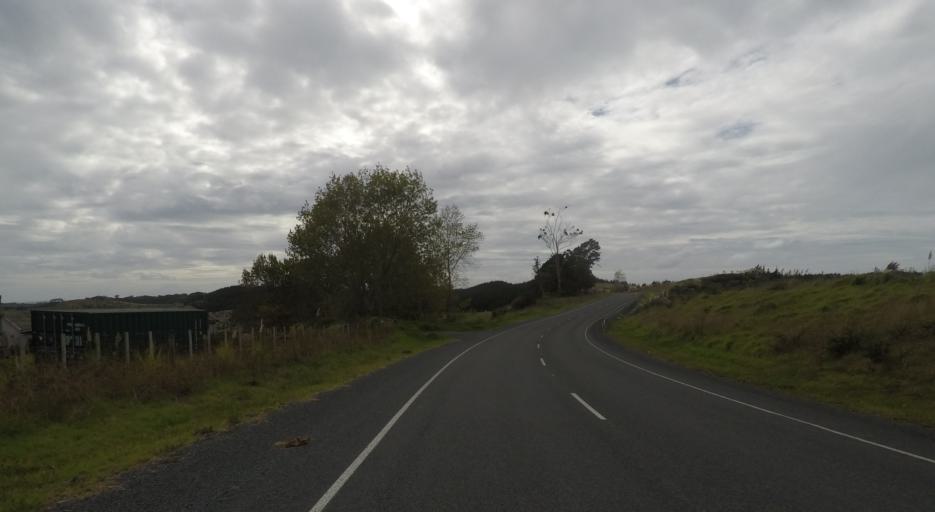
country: NZ
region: Auckland
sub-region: Auckland
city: Rothesay Bay
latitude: -36.6542
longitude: 174.6897
